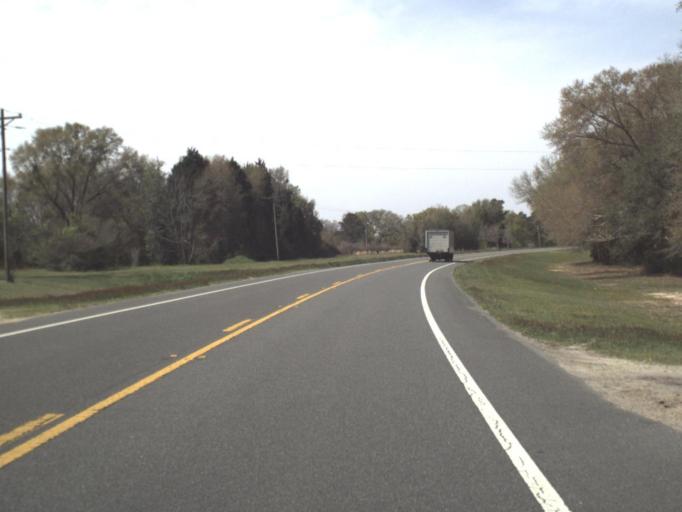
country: US
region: Florida
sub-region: Holmes County
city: Bonifay
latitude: 30.7621
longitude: -85.8609
